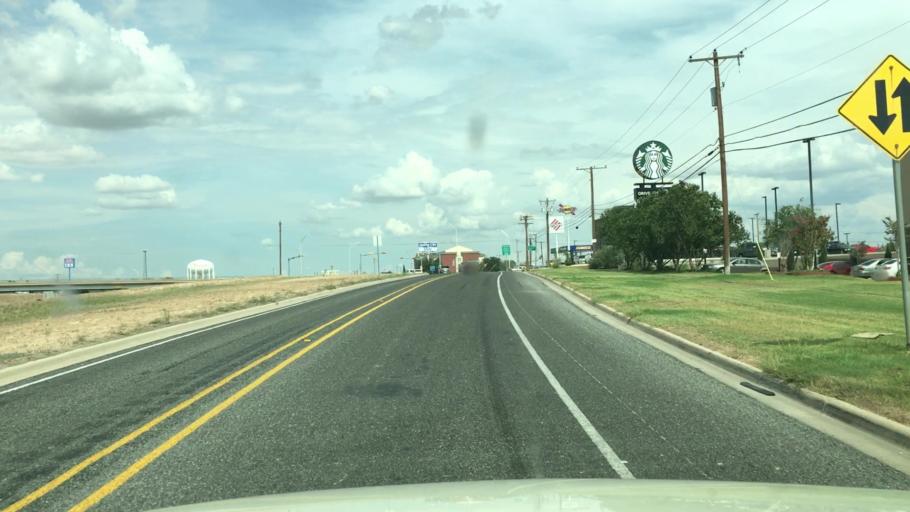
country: US
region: Texas
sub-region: Howard County
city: Big Spring
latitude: 32.2626
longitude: -101.4925
